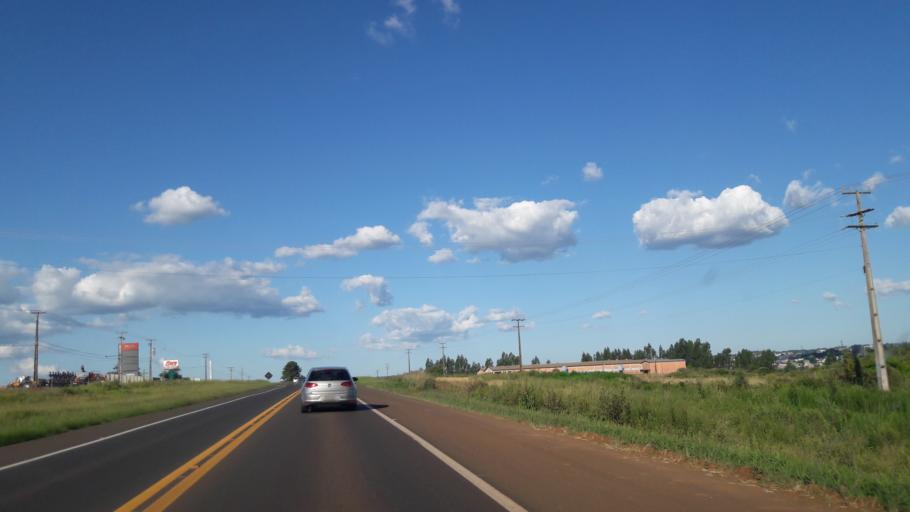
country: BR
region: Parana
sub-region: Guarapuava
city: Guarapuava
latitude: -25.3831
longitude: -51.5117
